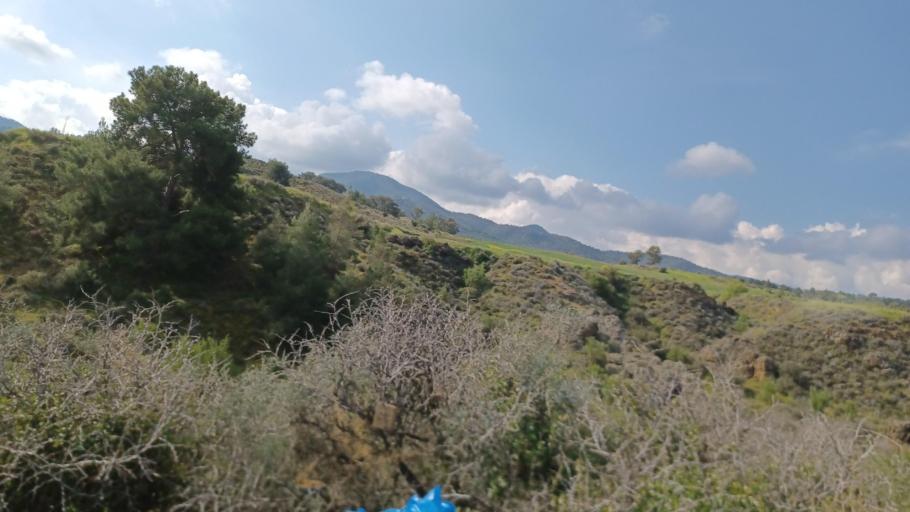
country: CY
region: Lefkosia
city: Astromeritis
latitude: 35.0815
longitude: 32.9535
